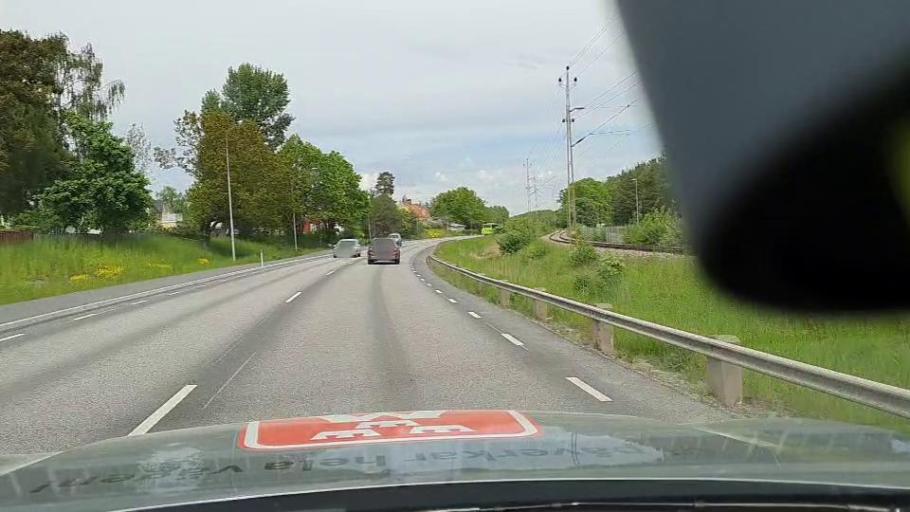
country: SE
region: Soedermanland
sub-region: Flens Kommun
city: Flen
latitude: 59.0698
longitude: 16.5914
